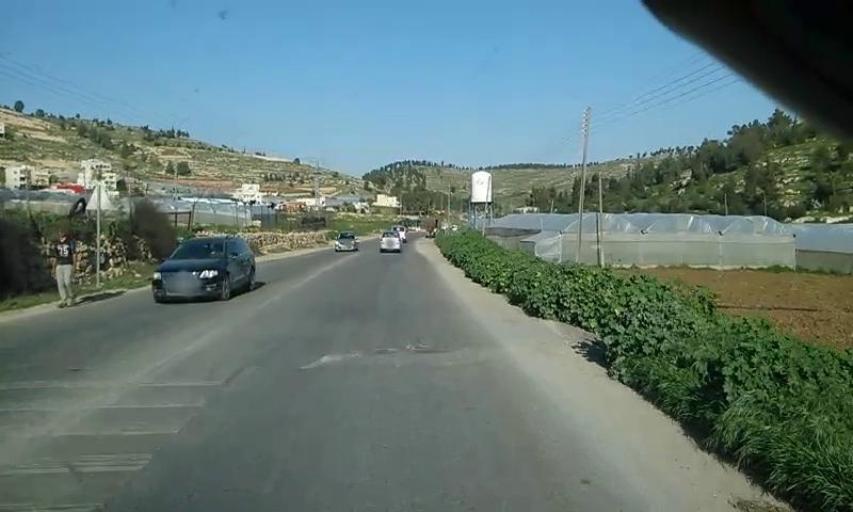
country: PS
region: West Bank
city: Ar Rihiyah
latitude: 31.4865
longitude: 35.0591
